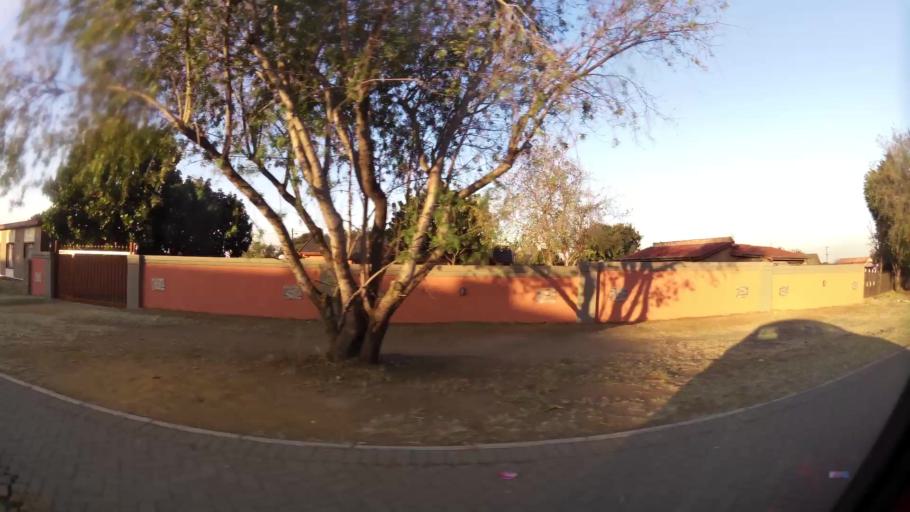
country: ZA
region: North-West
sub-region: Bojanala Platinum District Municipality
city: Rustenburg
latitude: -25.6411
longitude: 27.2089
